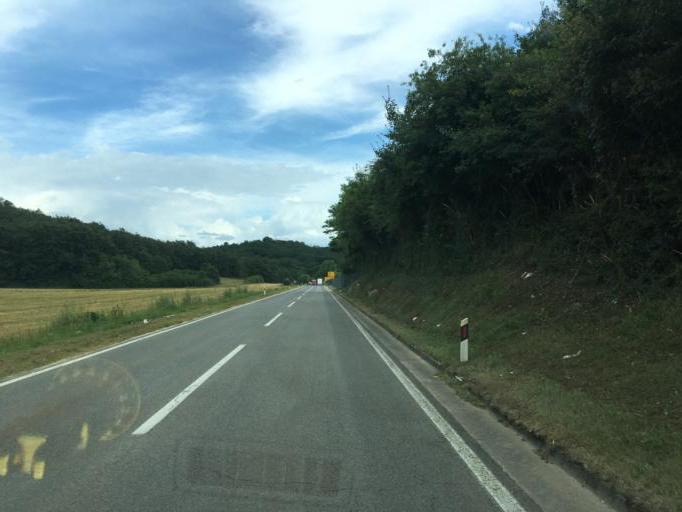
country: HR
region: Istarska
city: Pazin
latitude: 45.2427
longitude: 13.9059
